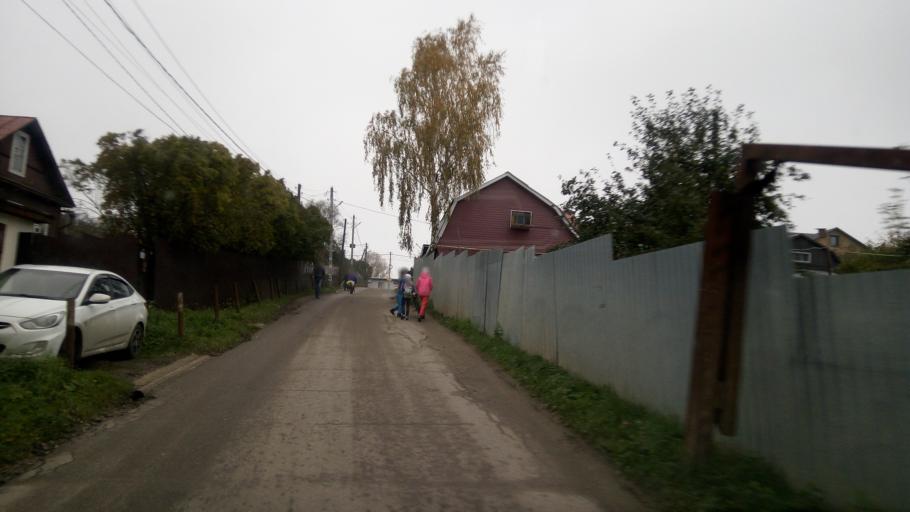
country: RU
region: Moskovskaya
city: Skhodnya
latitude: 55.9344
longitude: 37.2875
